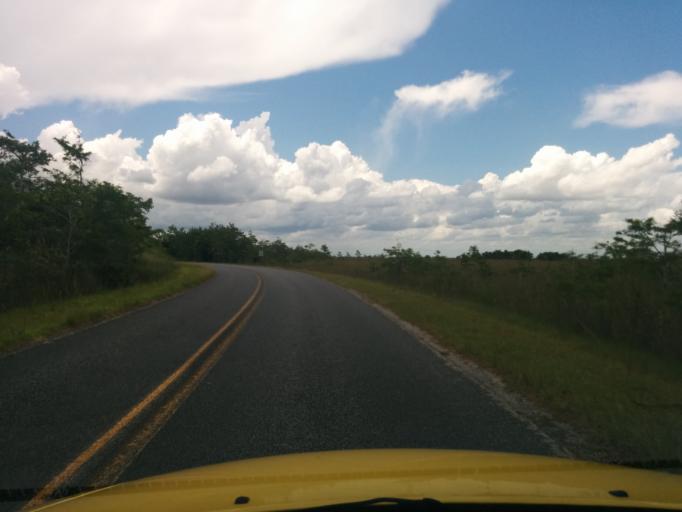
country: US
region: Florida
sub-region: Miami-Dade County
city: Florida City
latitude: 25.4383
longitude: -80.7817
